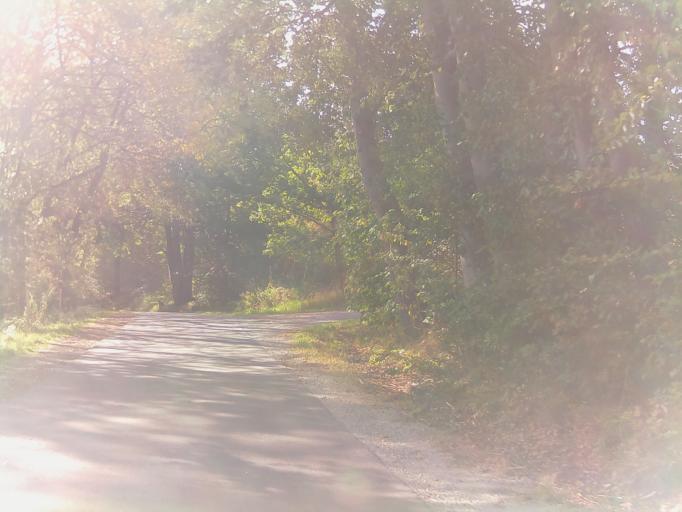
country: DE
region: Thuringia
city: Christes
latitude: 50.6586
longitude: 10.4672
